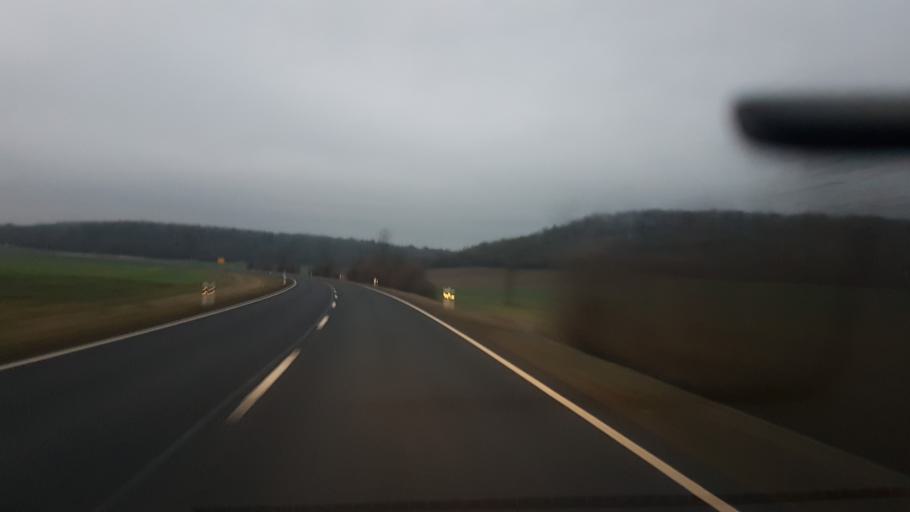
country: DE
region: Bavaria
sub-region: Regierungsbezirk Unterfranken
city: Ermershausen
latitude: 50.2439
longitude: 10.5689
